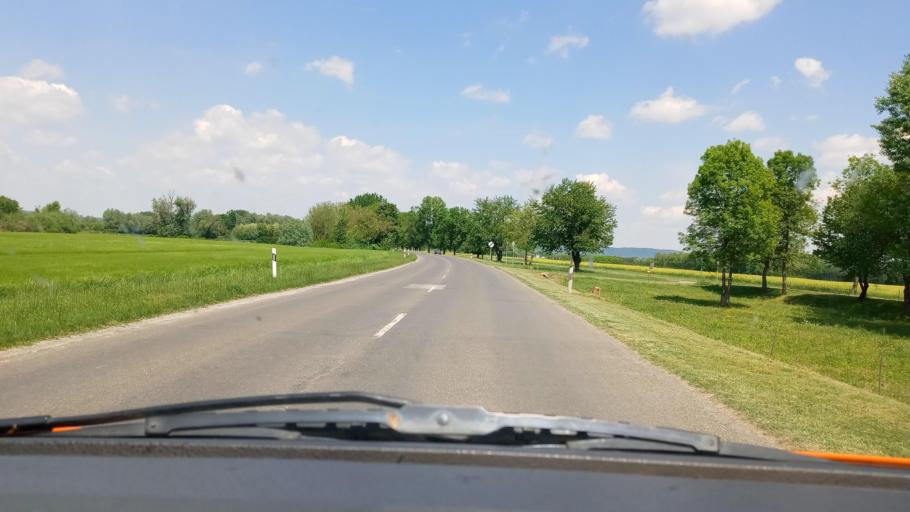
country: HU
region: Baranya
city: Harkany
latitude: 45.8106
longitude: 18.2135
